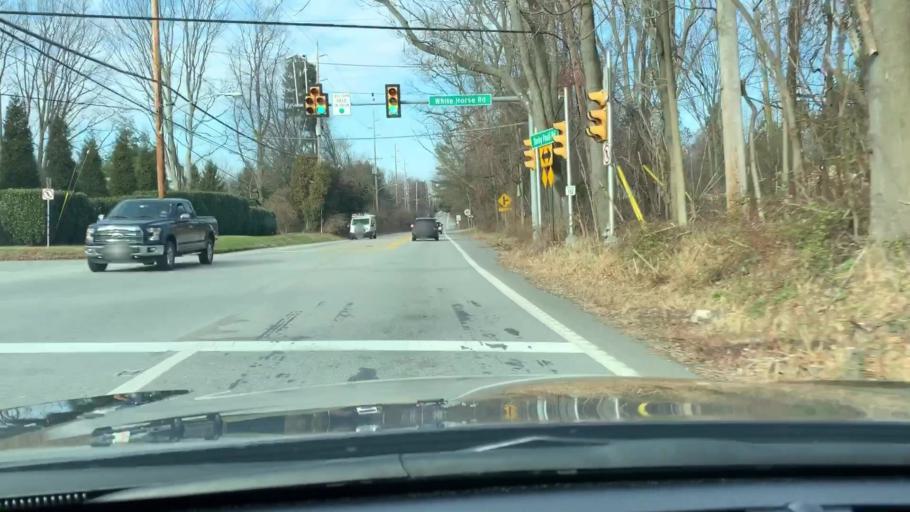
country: US
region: Pennsylvania
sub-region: Chester County
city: Berwyn
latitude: 40.0104
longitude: -75.4286
